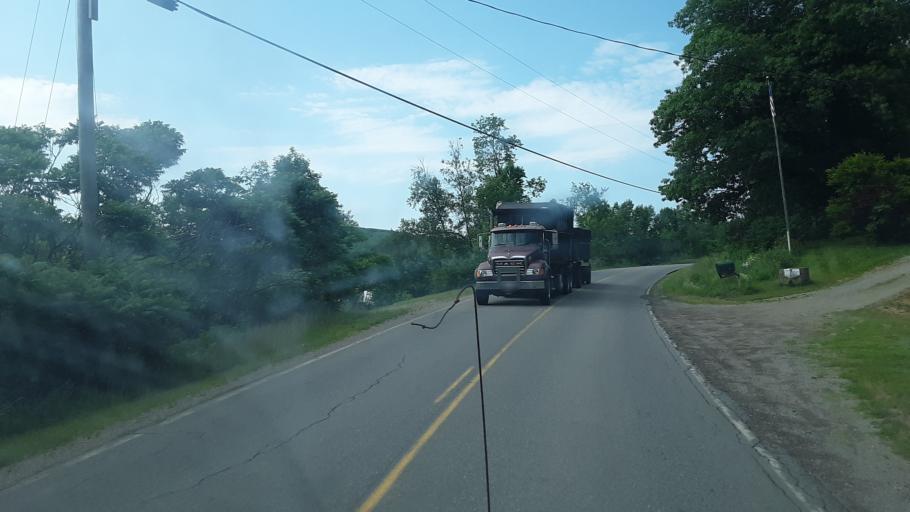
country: US
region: Maine
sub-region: Waldo County
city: Frankfort
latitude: 44.6053
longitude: -68.9364
